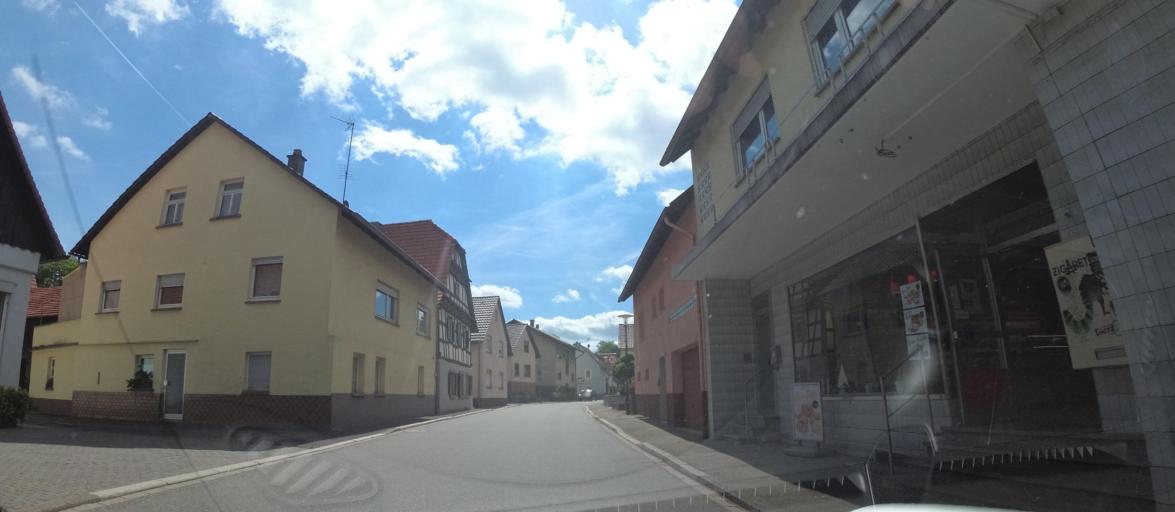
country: DE
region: Baden-Wuerttemberg
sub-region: Karlsruhe Region
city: Bretten
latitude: 49.0739
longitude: 8.7104
